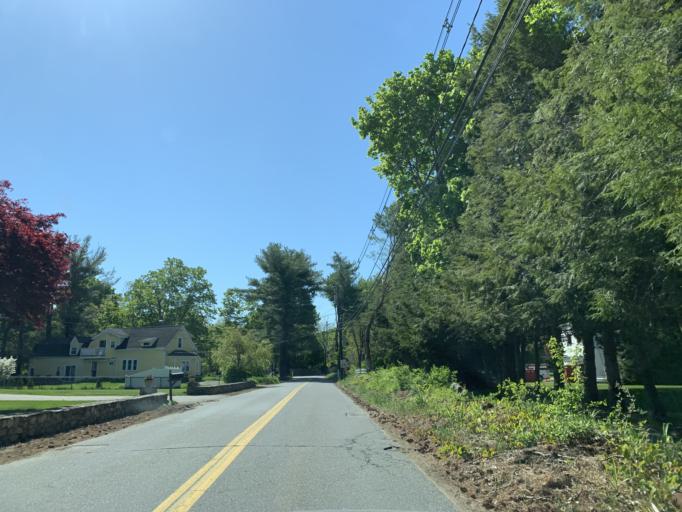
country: US
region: Massachusetts
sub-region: Middlesex County
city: Sudbury
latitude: 42.4151
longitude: -71.4126
